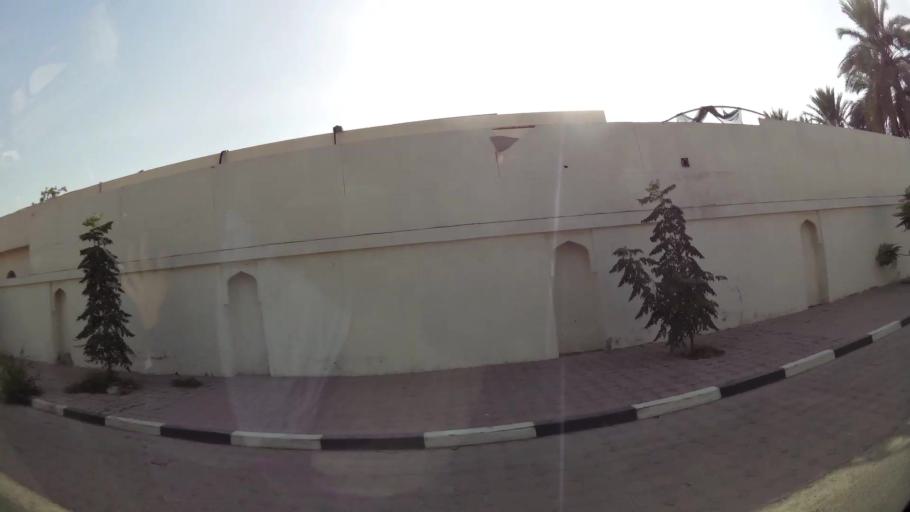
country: AE
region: Ash Shariqah
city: Sharjah
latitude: 25.2513
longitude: 55.4195
